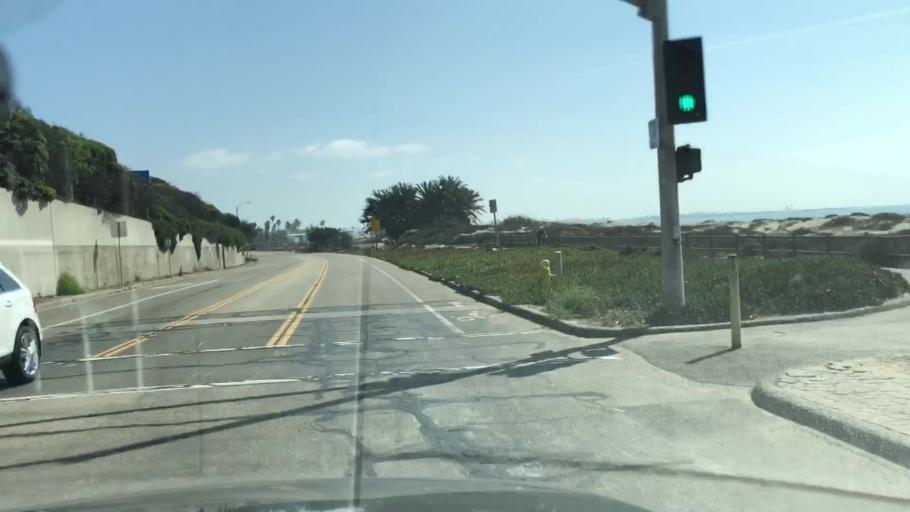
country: US
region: California
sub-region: Ventura County
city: Ventura
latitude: 34.2729
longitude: -119.2845
